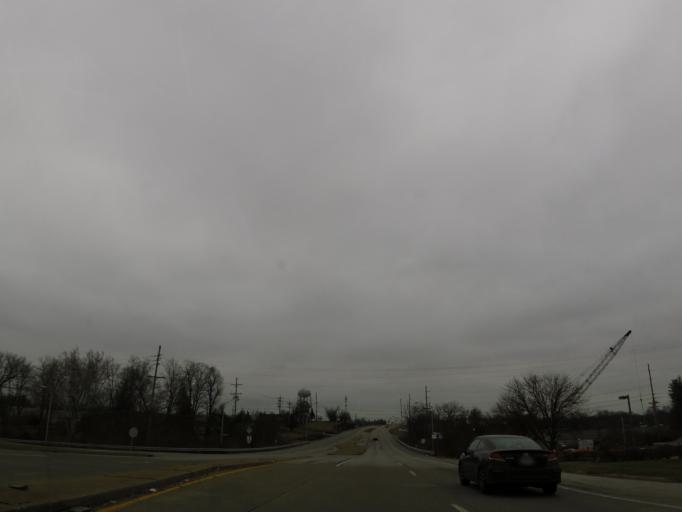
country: US
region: Kentucky
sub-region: Franklin County
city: Frankfort
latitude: 38.1796
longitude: -84.8948
